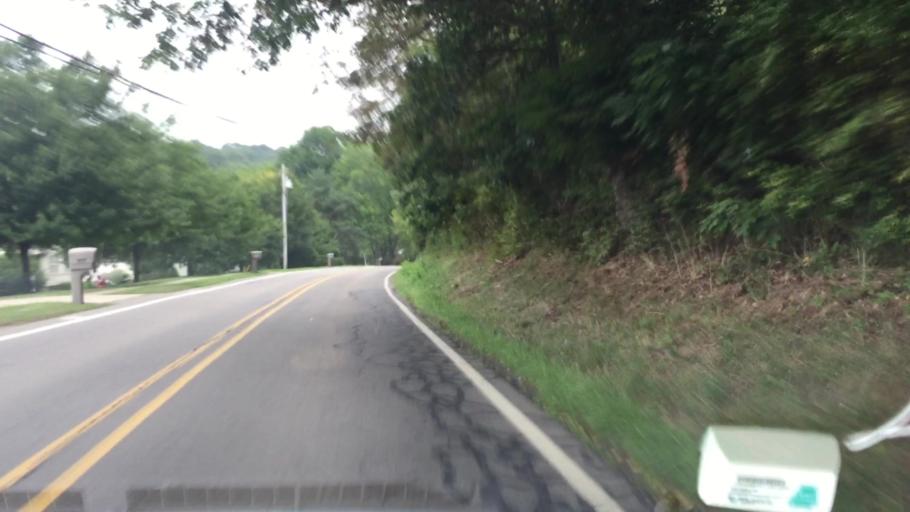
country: US
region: Pennsylvania
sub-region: Allegheny County
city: Franklin Park
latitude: 40.6044
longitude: -80.0745
